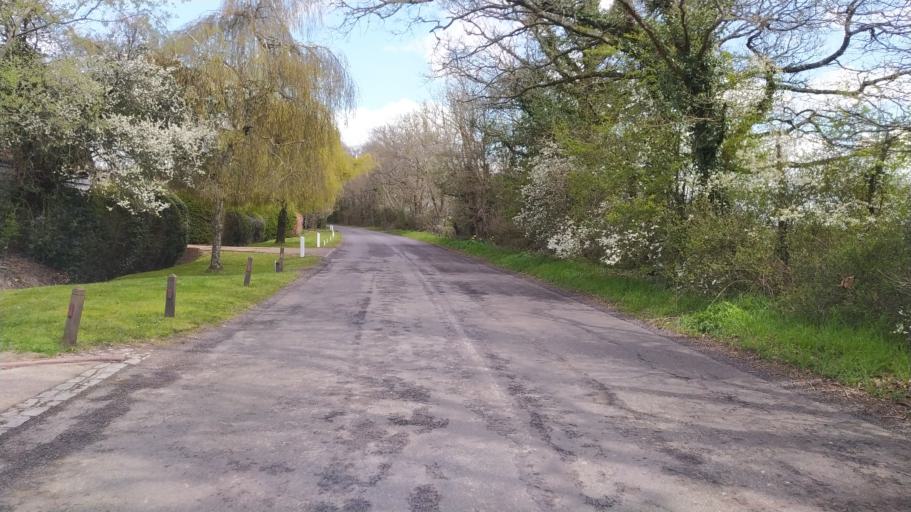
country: GB
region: England
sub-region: West Sussex
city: Petworth
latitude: 51.0330
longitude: -0.5715
